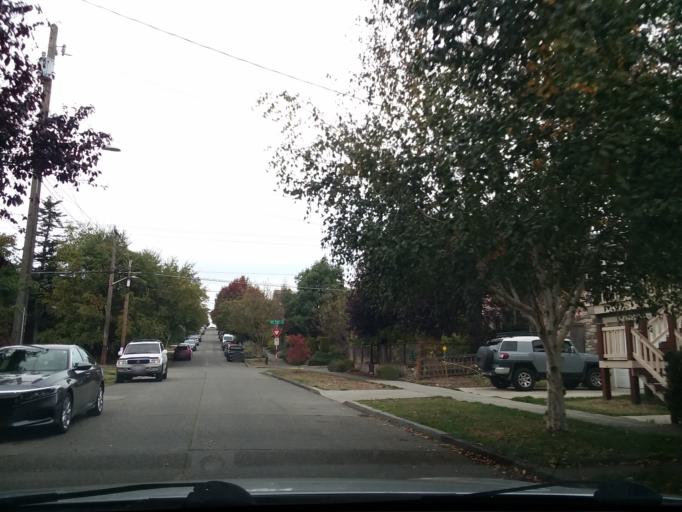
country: US
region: Washington
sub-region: King County
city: Shoreline
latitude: 47.6809
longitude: -122.3811
